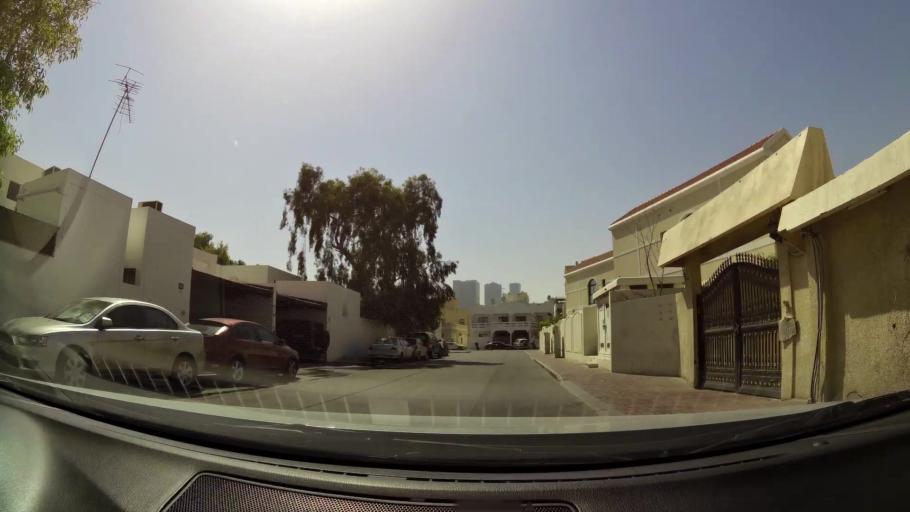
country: AE
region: Ash Shariqah
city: Sharjah
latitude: 25.2350
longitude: 55.2737
